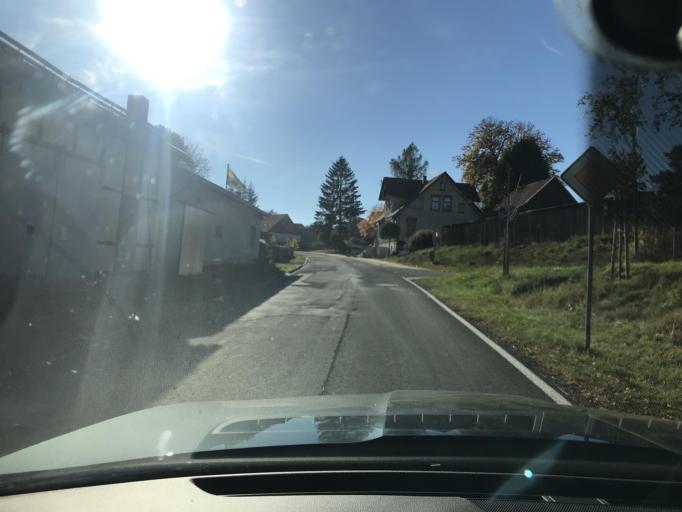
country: DE
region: Saxony-Anhalt
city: Friedrichsbrunn
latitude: 51.6818
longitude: 10.9718
